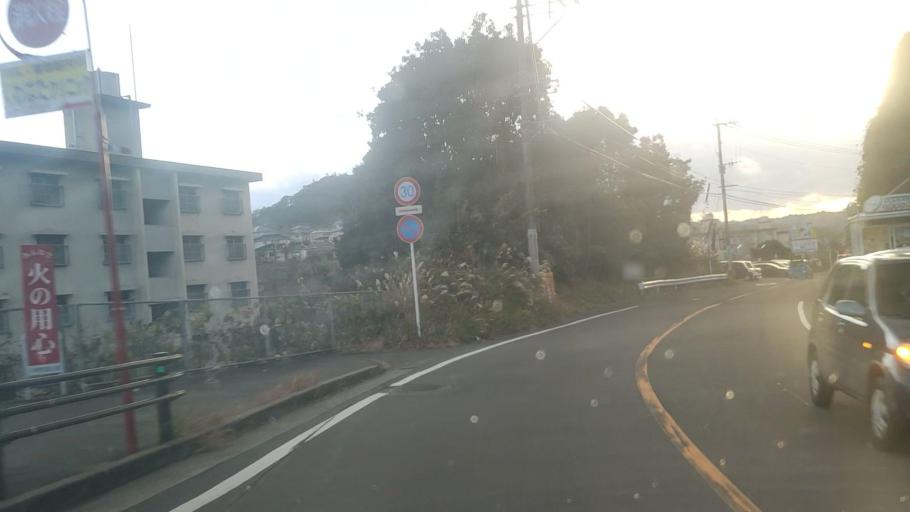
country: JP
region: Kagoshima
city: Kagoshima-shi
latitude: 31.6229
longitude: 130.5422
